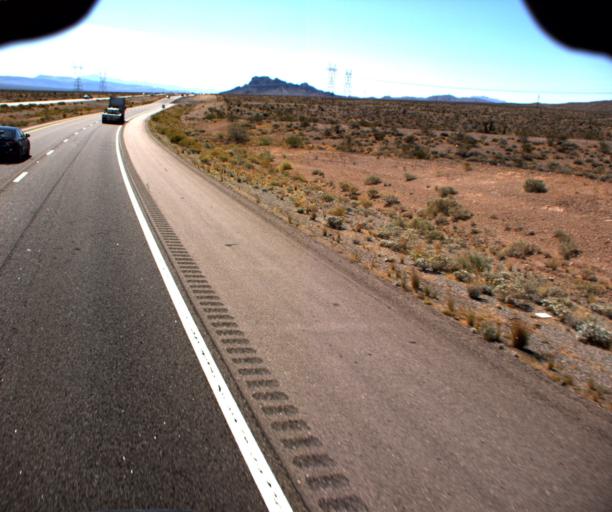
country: US
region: Nevada
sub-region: Clark County
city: Boulder City
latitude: 35.8432
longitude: -114.5738
